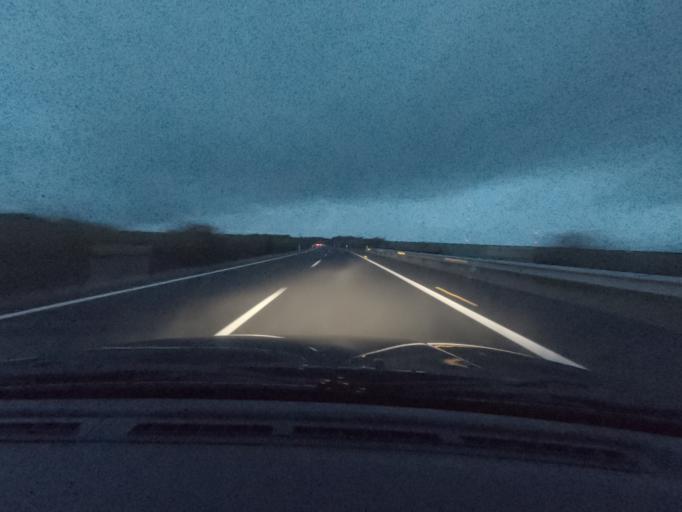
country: ES
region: Extremadura
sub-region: Provincia de Caceres
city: Aldea del Cano
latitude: 39.3363
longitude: -6.3353
